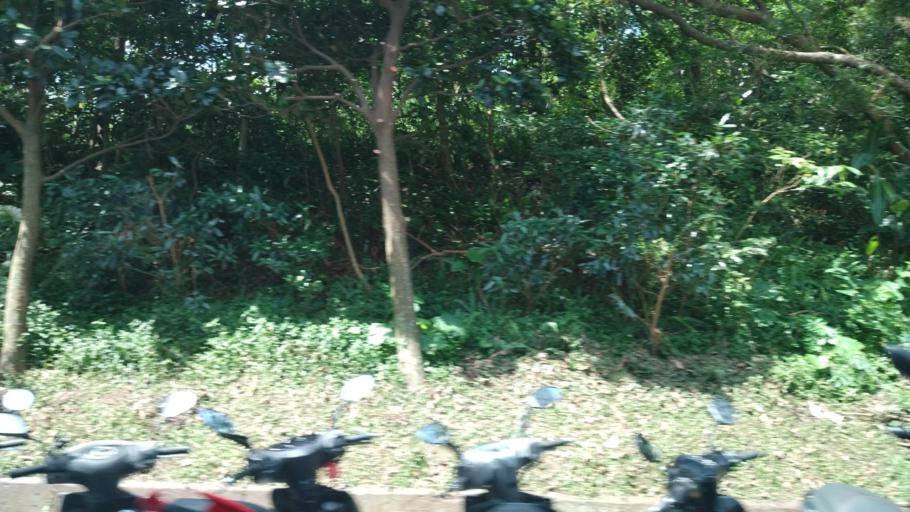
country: TW
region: Taipei
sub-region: Taipei
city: Banqiao
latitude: 24.9381
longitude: 121.5029
